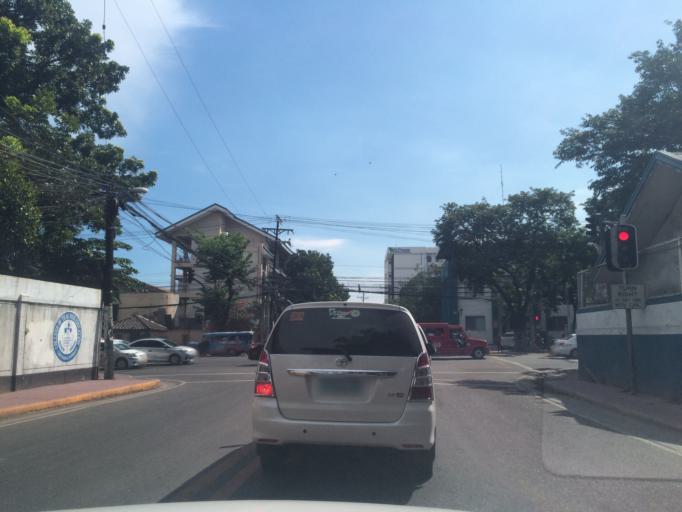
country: PH
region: Central Visayas
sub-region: Cebu City
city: Calero
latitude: 10.3023
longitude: 123.8963
